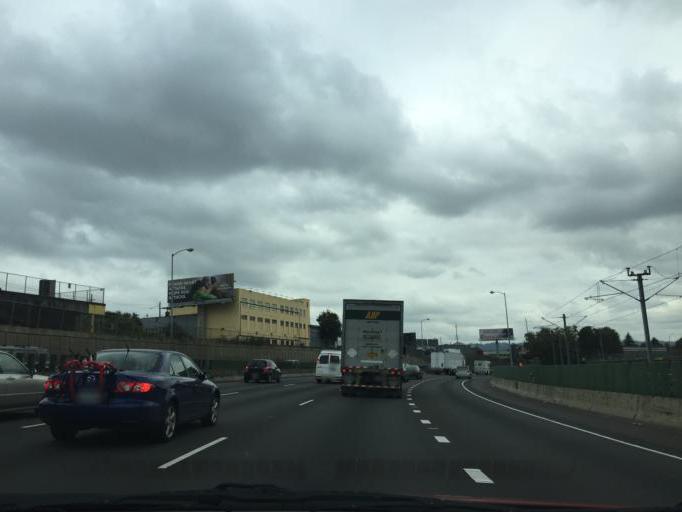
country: US
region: Oregon
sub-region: Multnomah County
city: Portland
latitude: 45.5316
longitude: -122.6339
